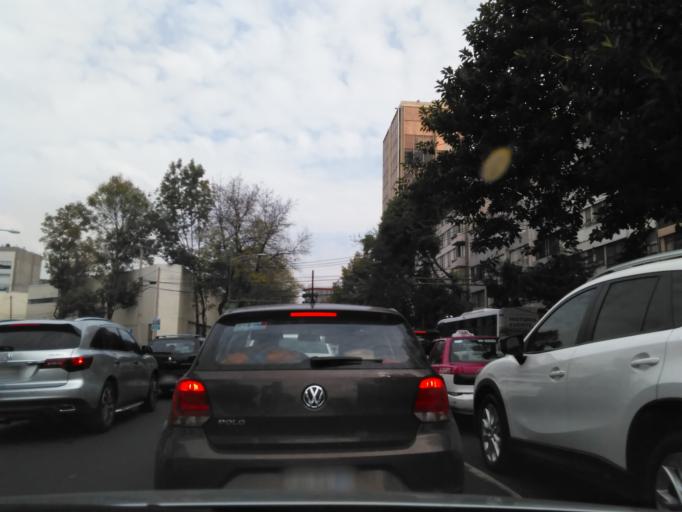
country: MX
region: Mexico City
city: Colonia del Valle
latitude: 19.3824
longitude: -99.1779
